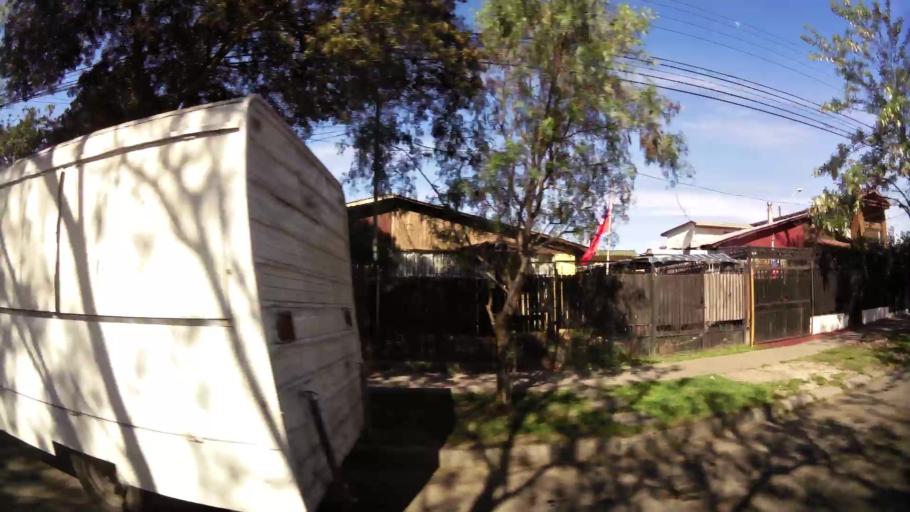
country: CL
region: Santiago Metropolitan
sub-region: Provincia de Santiago
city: Lo Prado
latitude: -33.5004
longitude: -70.7376
